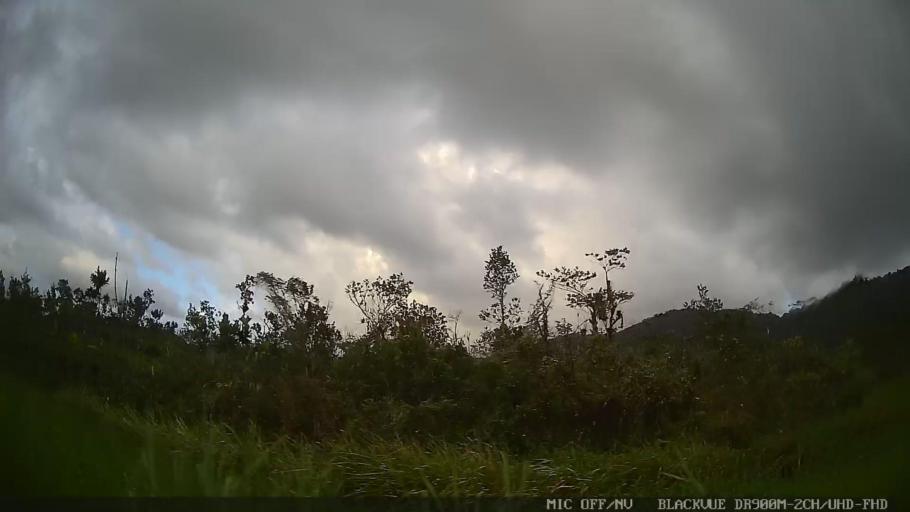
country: BR
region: Sao Paulo
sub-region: Itanhaem
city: Itanhaem
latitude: -24.1359
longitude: -46.7780
